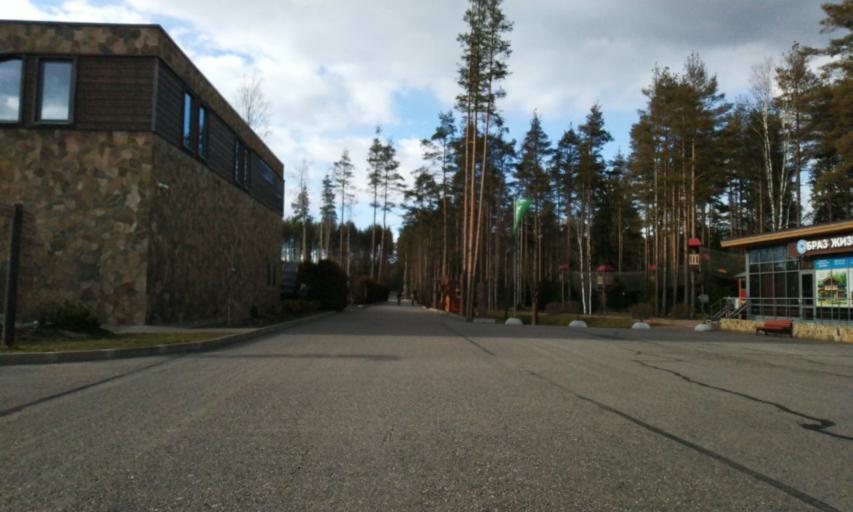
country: RU
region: Leningrad
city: Novoye Devyatkino
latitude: 60.1278
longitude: 30.4459
